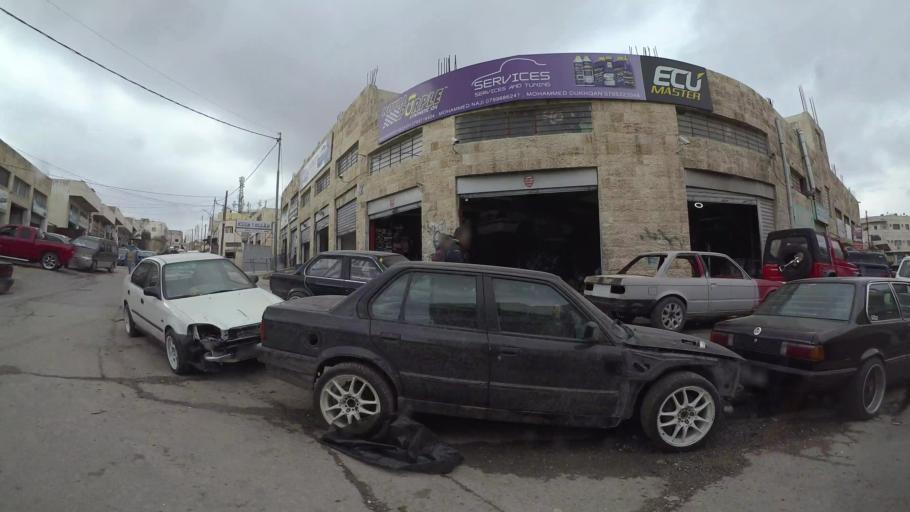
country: JO
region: Amman
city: Wadi as Sir
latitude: 31.9437
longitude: 35.8376
